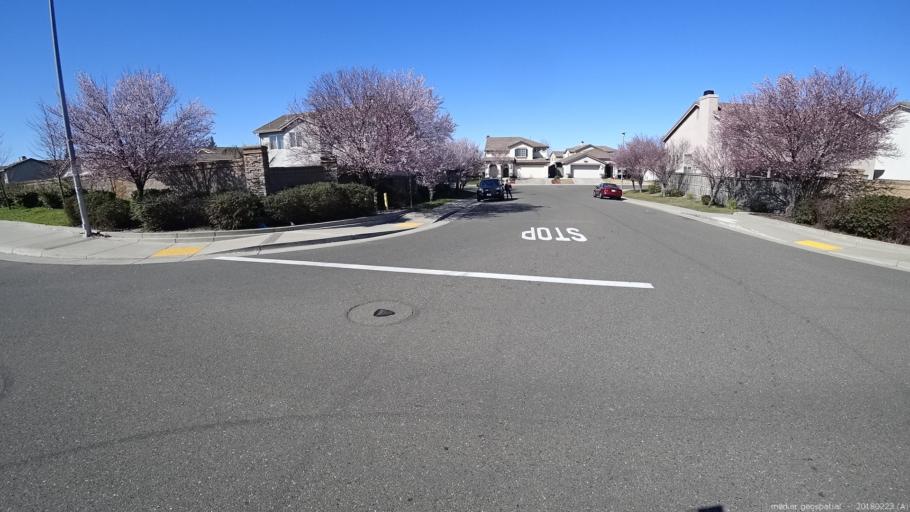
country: US
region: California
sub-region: Sacramento County
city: Antelope
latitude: 38.7045
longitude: -121.3533
